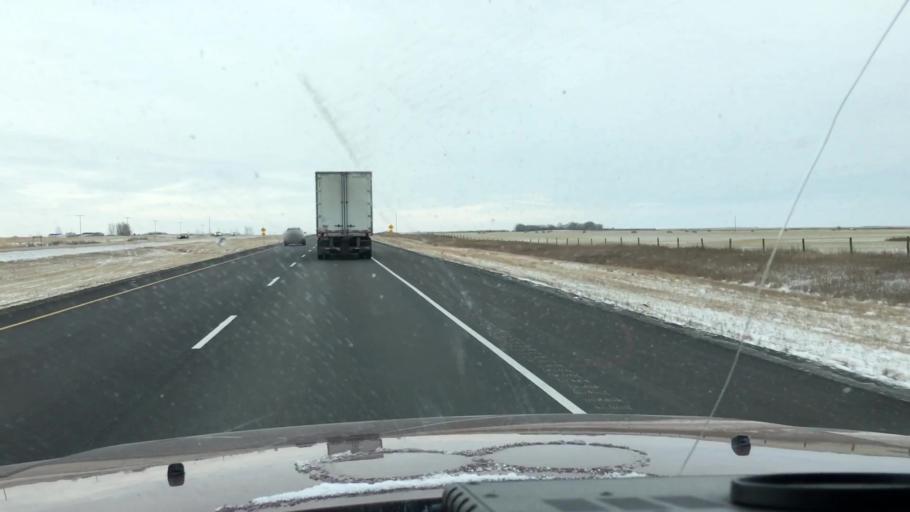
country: CA
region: Saskatchewan
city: Saskatoon
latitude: 51.7939
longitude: -106.4856
